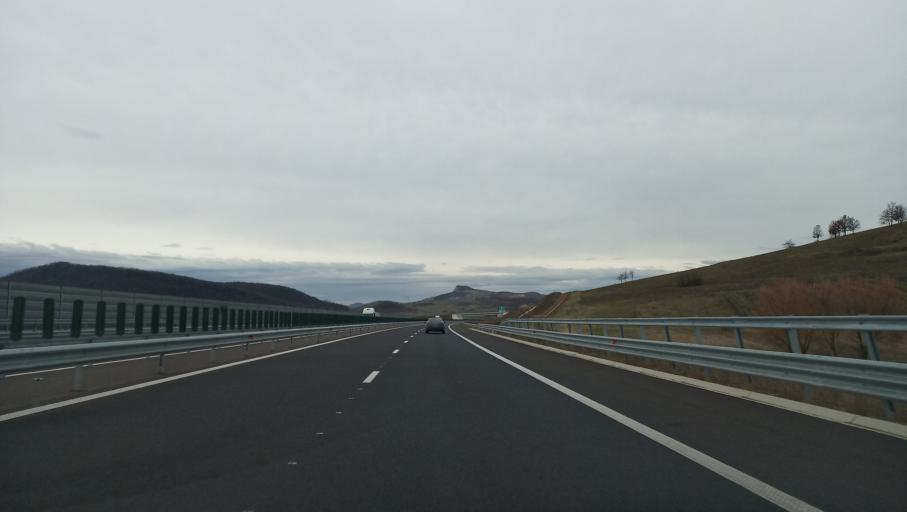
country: RO
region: Hunedoara
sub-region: Comuna Branisca
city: Branisca
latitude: 45.9268
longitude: 22.7705
